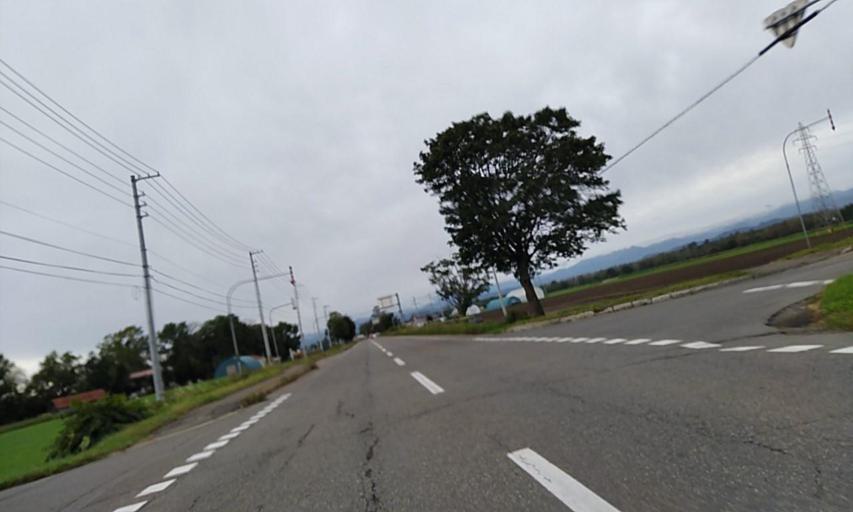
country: JP
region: Hokkaido
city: Obihiro
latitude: 42.7193
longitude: 143.1487
